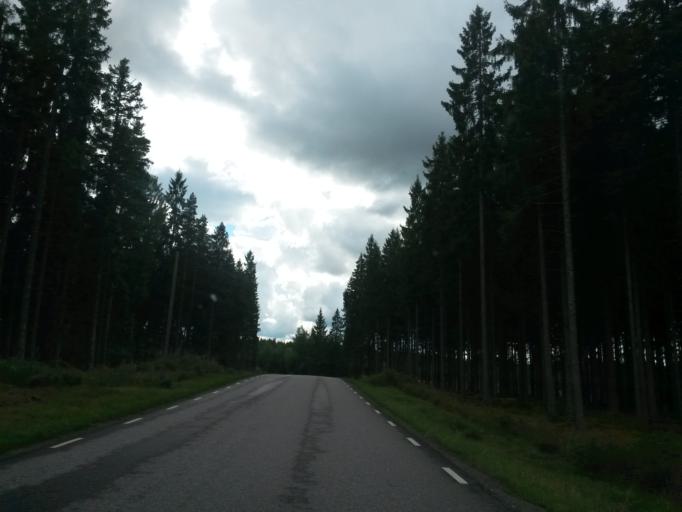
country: SE
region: Vaestra Goetaland
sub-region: Herrljunga Kommun
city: Herrljunga
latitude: 58.0034
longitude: 13.0354
